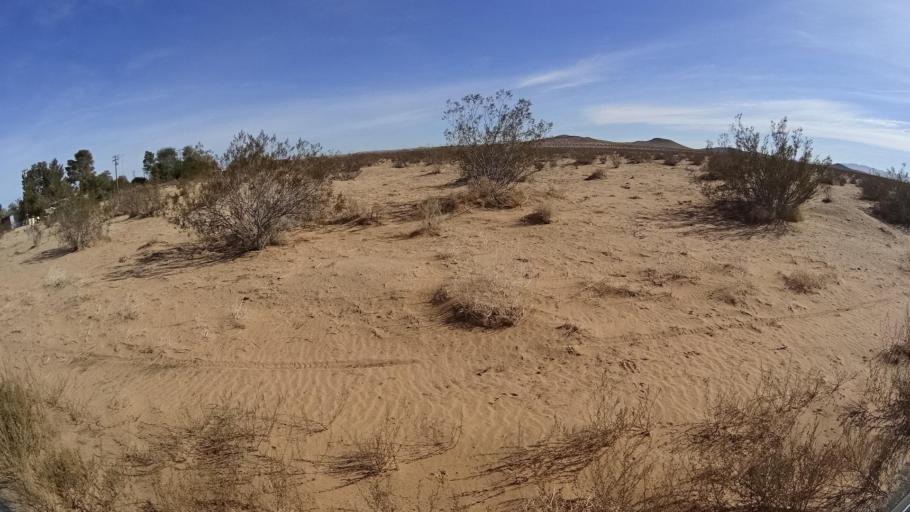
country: US
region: California
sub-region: Kern County
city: North Edwards
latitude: 35.0870
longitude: -117.7927
